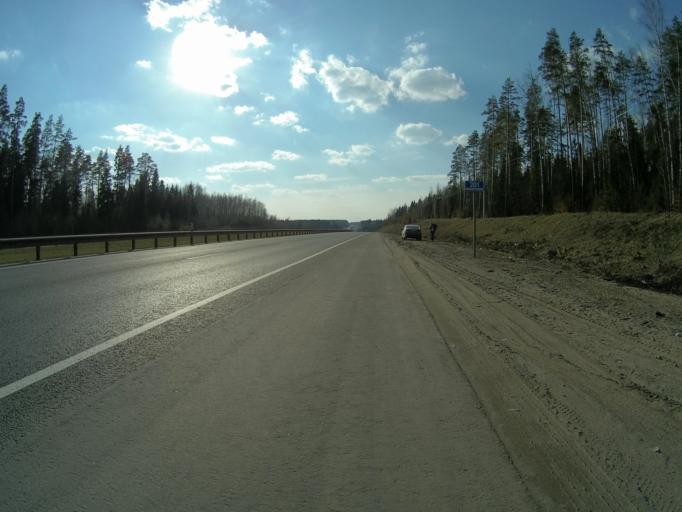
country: RU
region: Vladimir
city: Orgtrud
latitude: 56.1038
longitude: 40.6693
